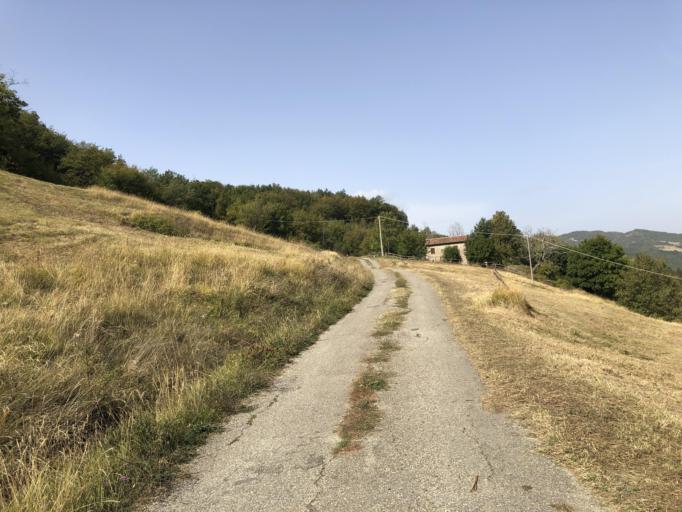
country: IT
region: Emilia-Romagna
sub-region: Forli-Cesena
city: Portico e San Benedetto
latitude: 44.0157
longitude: 11.7870
